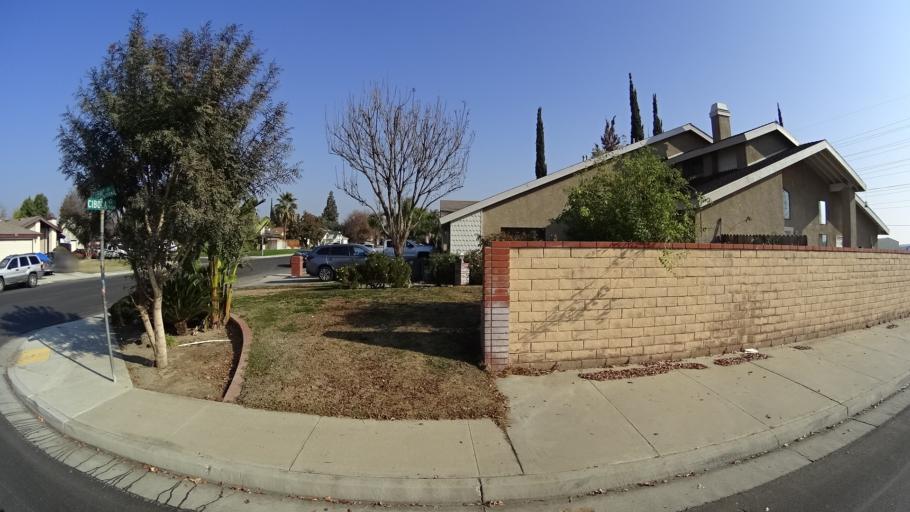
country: US
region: California
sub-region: Kern County
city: Greenacres
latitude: 35.3186
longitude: -119.0864
